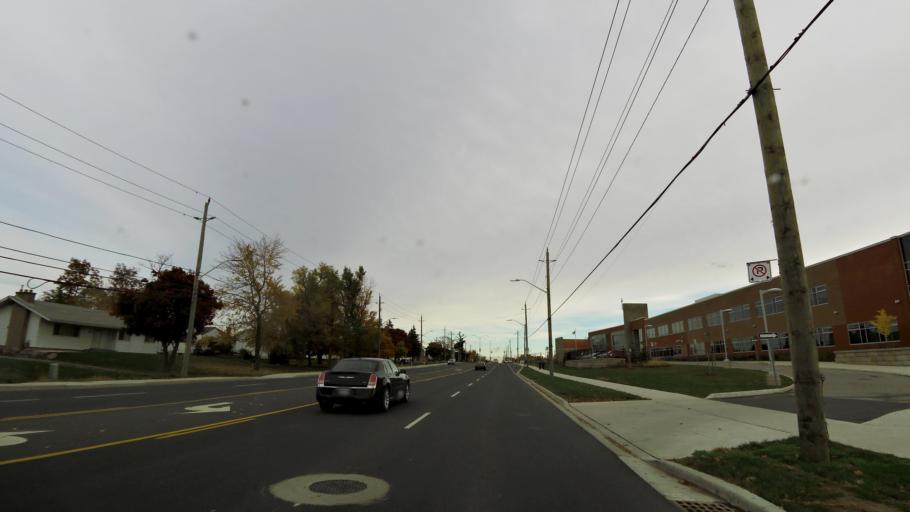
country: CA
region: Ontario
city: Hamilton
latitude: 43.1824
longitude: -79.8175
